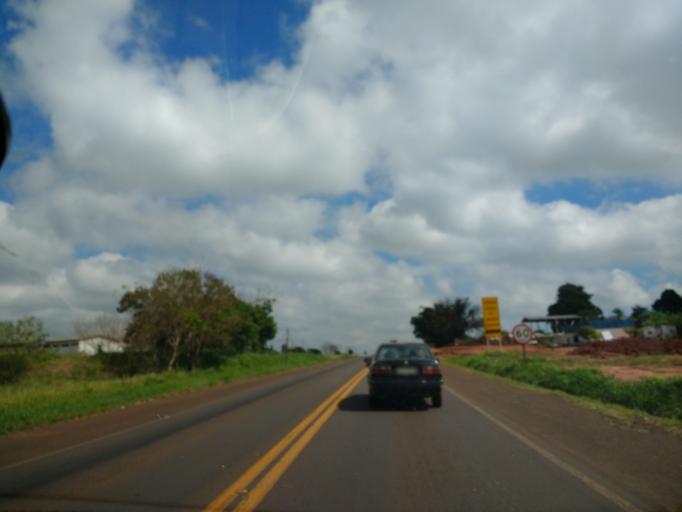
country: BR
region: Parana
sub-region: Cruzeiro Do Oeste
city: Cruzeiro do Oeste
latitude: -23.7983
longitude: -53.0531
